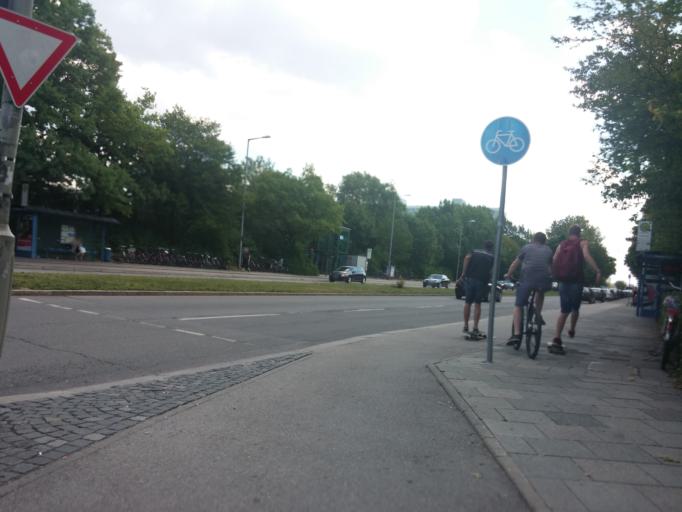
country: DE
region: Bavaria
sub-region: Upper Bavaria
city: Neubiberg
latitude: 48.1090
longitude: 11.6462
